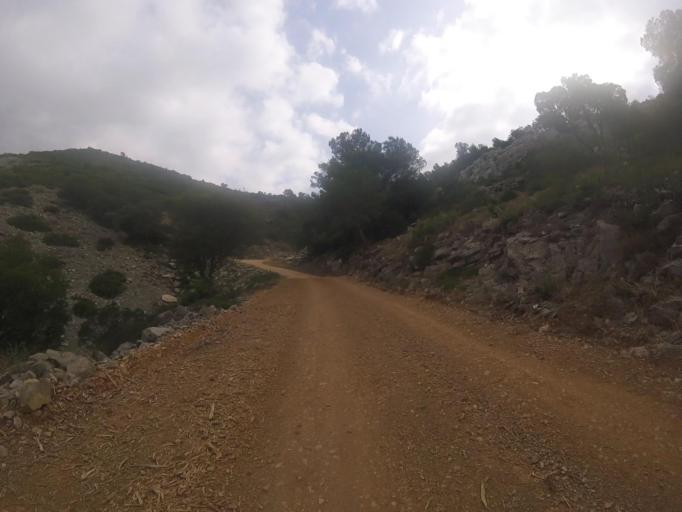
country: ES
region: Valencia
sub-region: Provincia de Castello
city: Santa Magdalena de Pulpis
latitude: 40.3458
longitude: 0.3217
